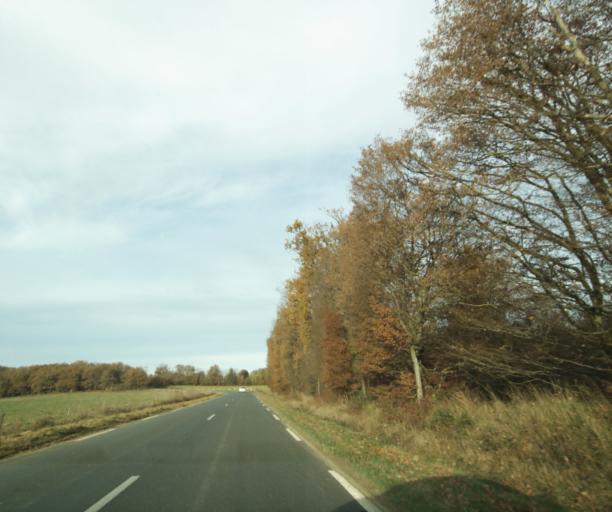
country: FR
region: Midi-Pyrenees
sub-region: Departement du Gers
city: Eauze
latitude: 43.8181
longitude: 0.0966
